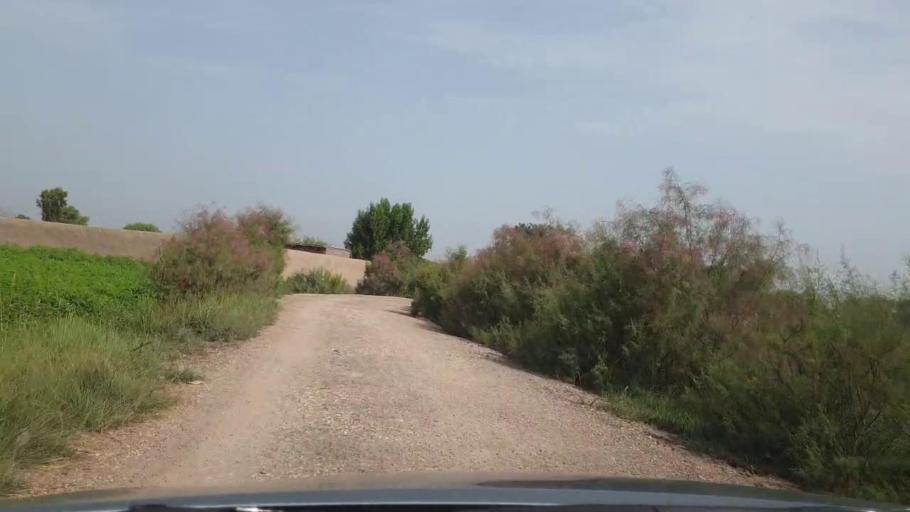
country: PK
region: Sindh
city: Rohri
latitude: 27.6499
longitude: 69.0232
